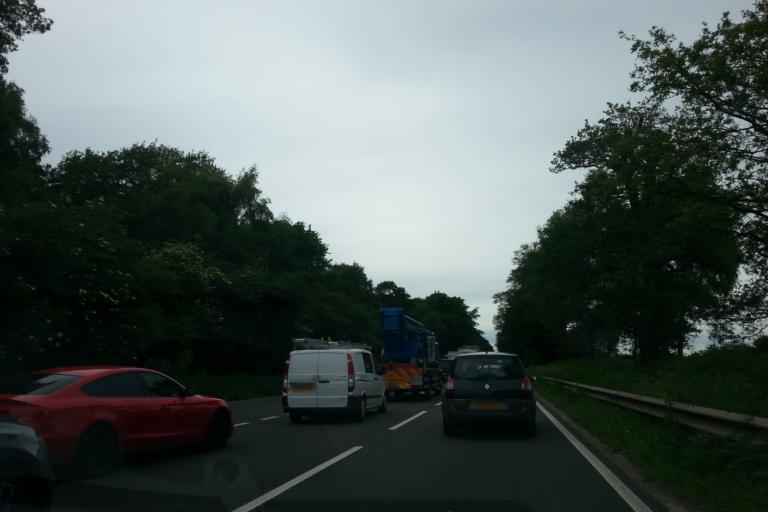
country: GB
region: England
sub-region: Solihull
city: Chelmsley Wood
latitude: 52.4686
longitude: -1.7053
